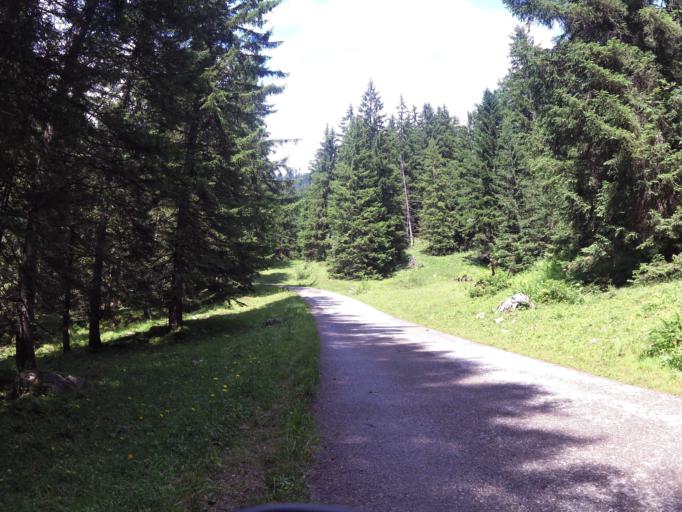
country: AT
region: Tyrol
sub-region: Politischer Bezirk Kitzbuhel
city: Waidring
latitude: 47.6649
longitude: 12.5896
